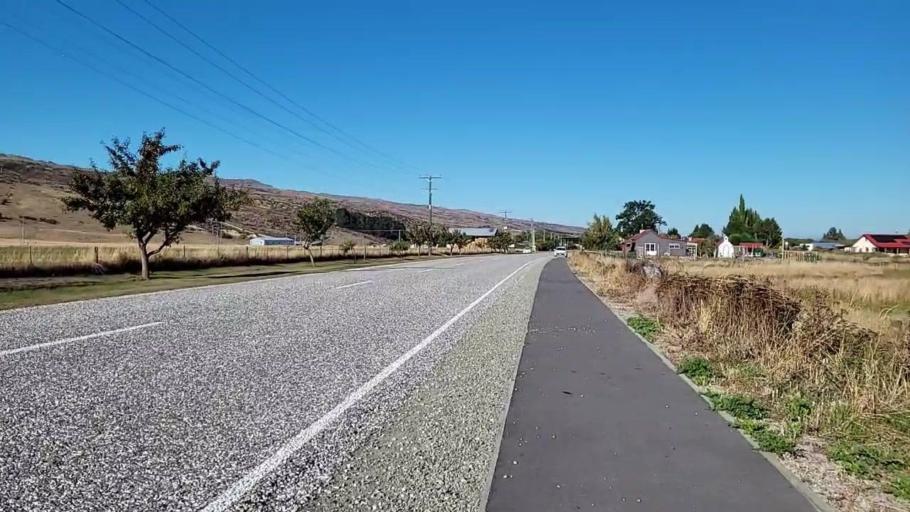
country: NZ
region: Otago
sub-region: Queenstown-Lakes District
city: Wanaka
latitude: -45.0036
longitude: 169.9163
